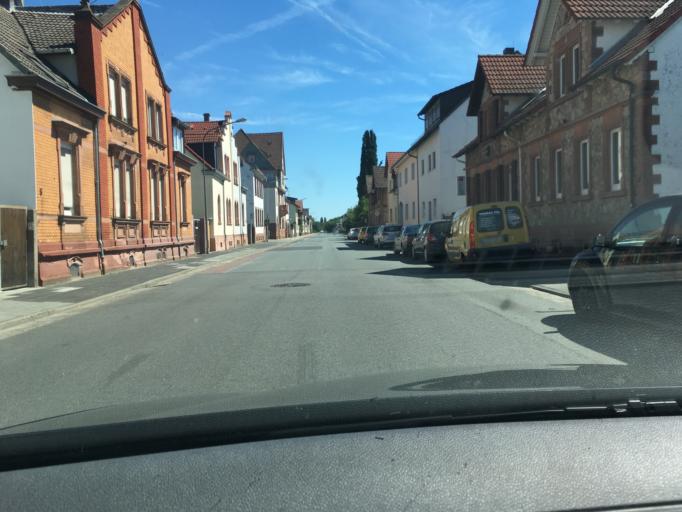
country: DE
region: Hesse
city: Dieburg
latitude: 49.8996
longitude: 8.8473
